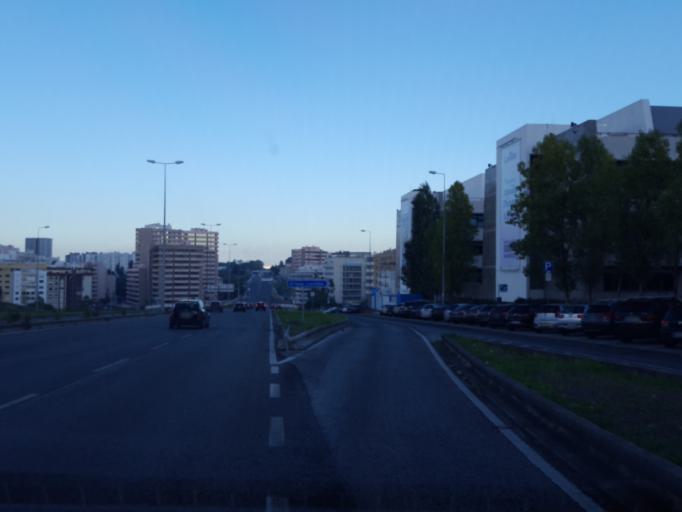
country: PT
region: Lisbon
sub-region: Odivelas
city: Pontinha
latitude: 38.7498
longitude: -9.1768
